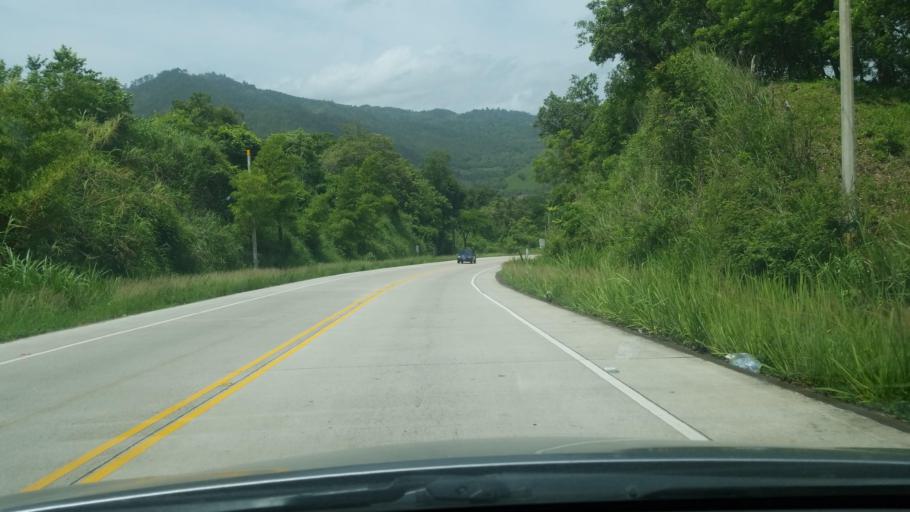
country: HN
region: Copan
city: Quezailica
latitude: 14.8966
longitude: -88.7588
